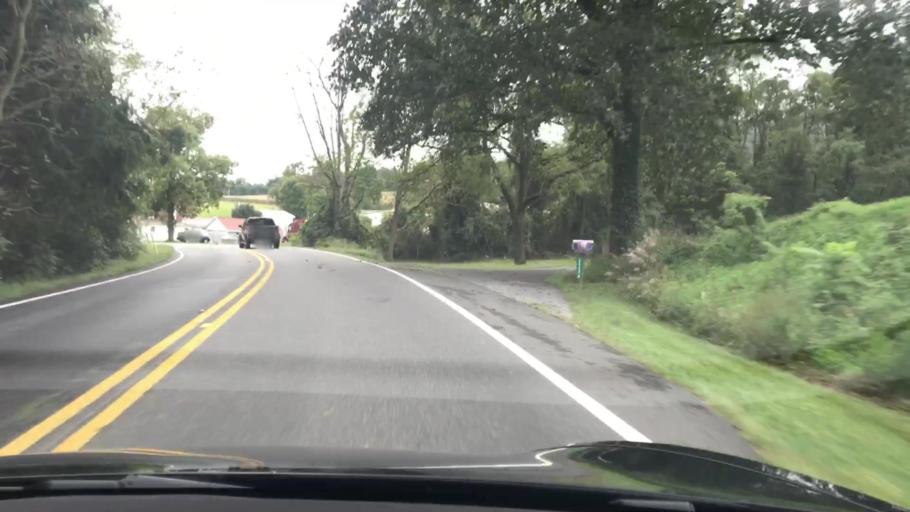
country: US
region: Pennsylvania
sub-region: York County
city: Dillsburg
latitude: 40.0782
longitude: -77.0866
